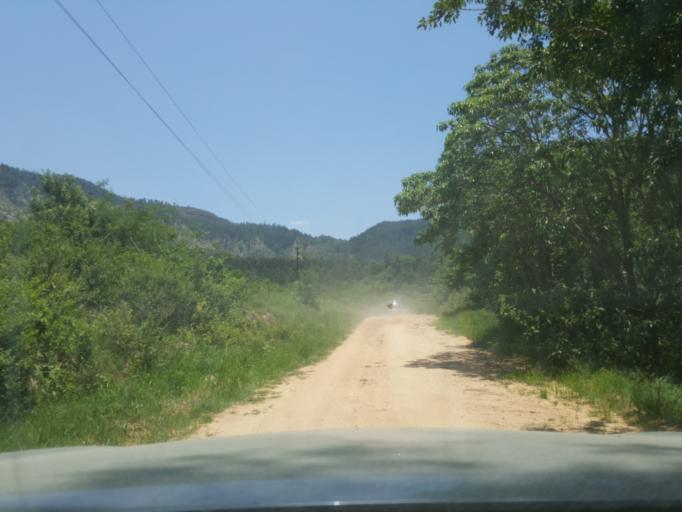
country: ZA
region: Limpopo
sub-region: Mopani District Municipality
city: Hoedspruit
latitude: -24.5967
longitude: 30.8902
